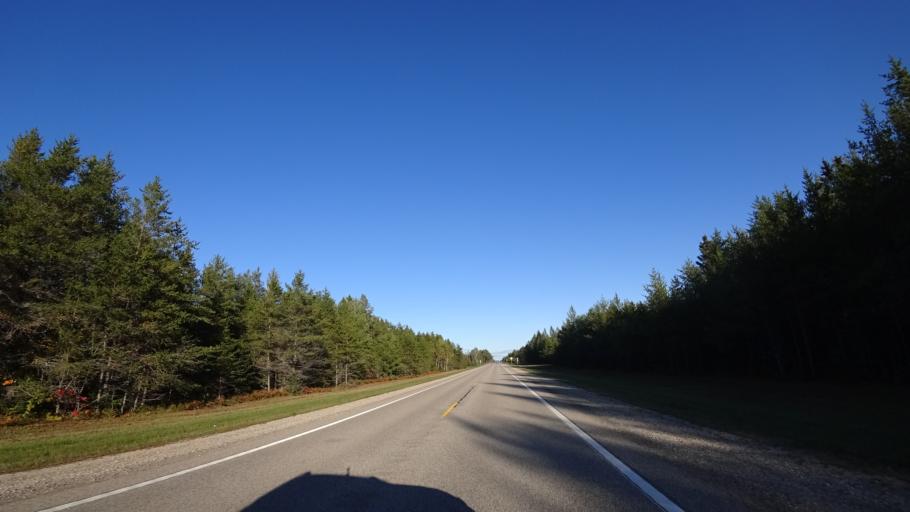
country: US
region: Michigan
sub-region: Alger County
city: Munising
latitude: 46.3462
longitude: -86.2821
